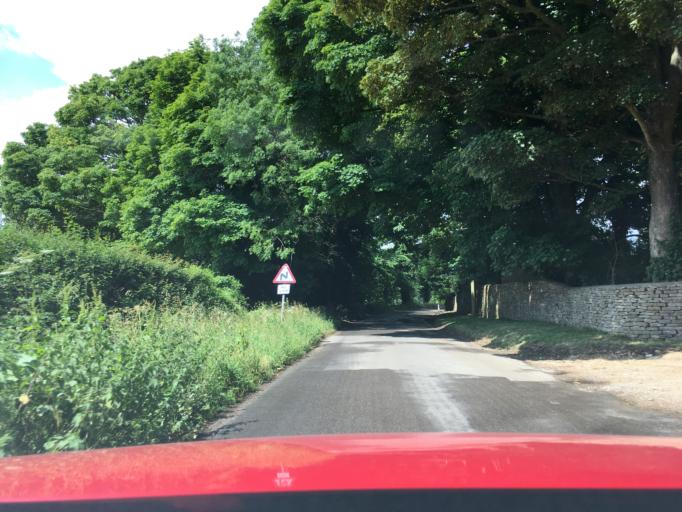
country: GB
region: England
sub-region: Gloucestershire
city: Chalford
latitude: 51.6848
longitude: -2.1429
